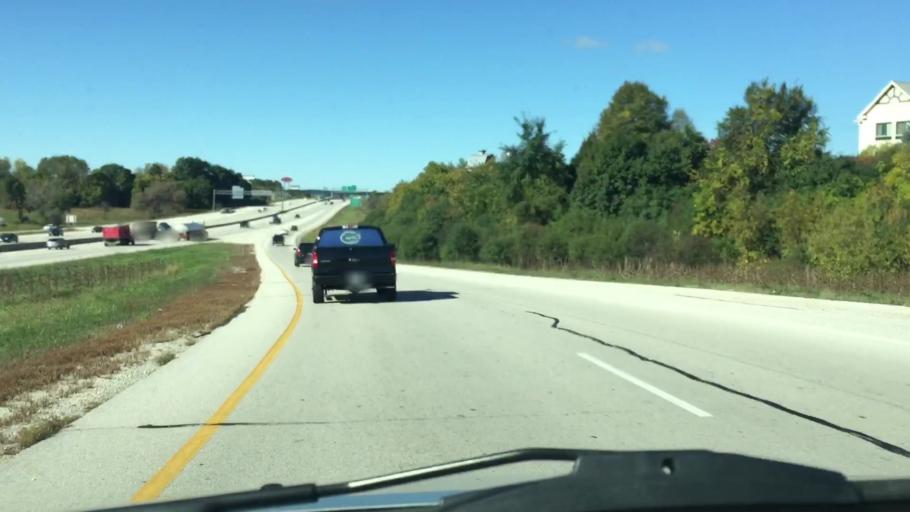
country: US
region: Wisconsin
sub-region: Waukesha County
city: Waukesha
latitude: 43.0498
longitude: -88.2270
